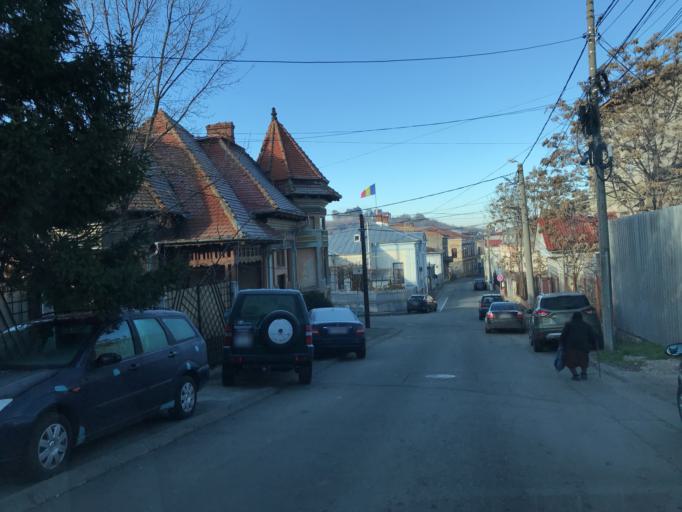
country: RO
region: Olt
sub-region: Municipiul Slatina
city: Slatina
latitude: 44.4286
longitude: 24.3598
